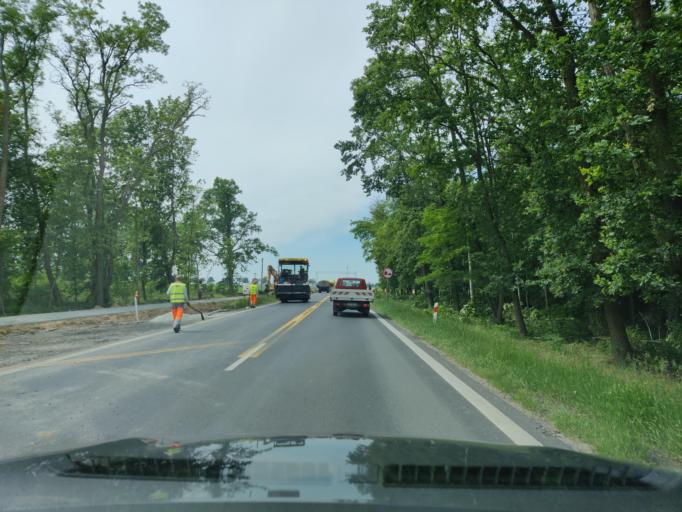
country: PL
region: Greater Poland Voivodeship
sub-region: Powiat grodziski
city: Granowo
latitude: 52.2266
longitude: 16.5894
